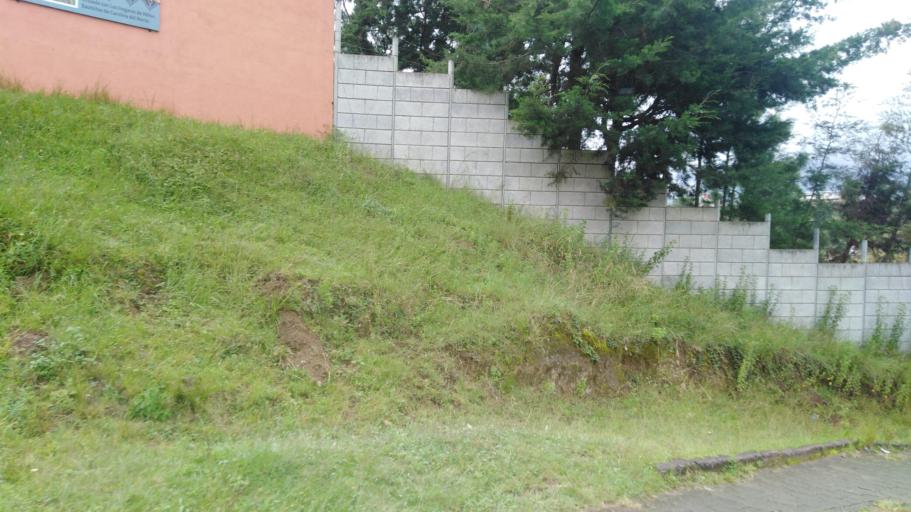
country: GT
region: Quetzaltenango
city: Quetzaltenango
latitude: 14.8567
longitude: -91.5050
